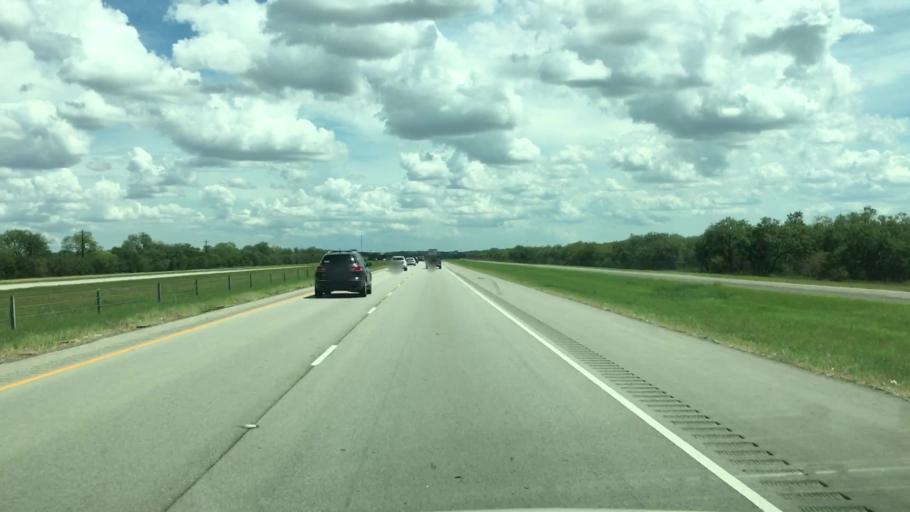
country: US
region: Texas
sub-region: Live Oak County
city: George West
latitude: 28.2783
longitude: -97.9531
